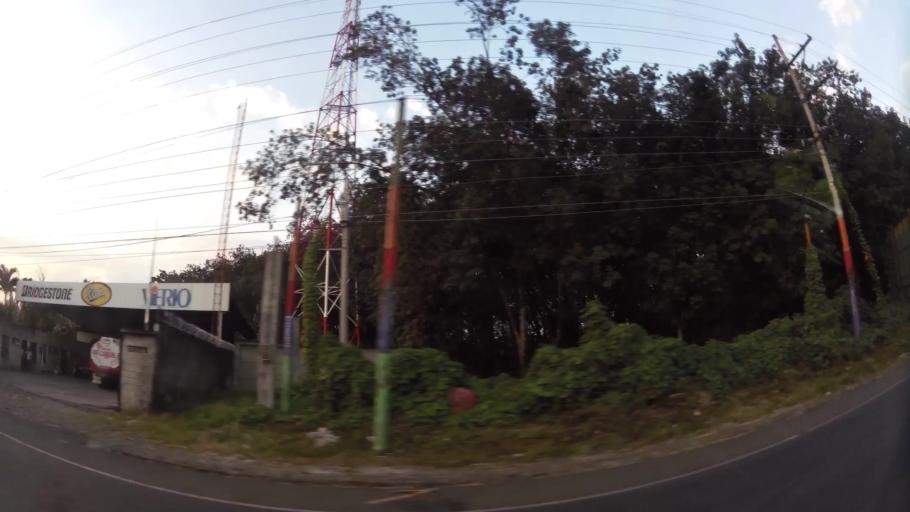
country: GT
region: Retalhuleu
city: San Sebastian
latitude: 14.5755
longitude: -91.6398
